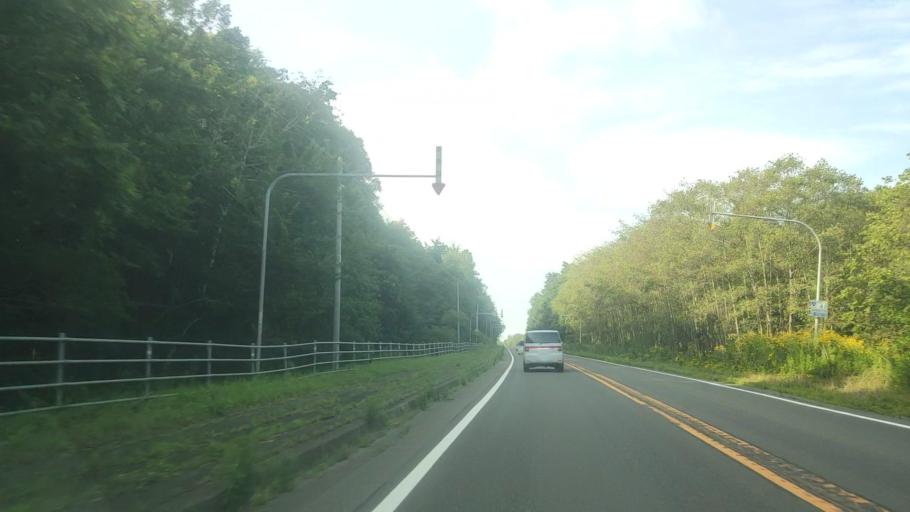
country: JP
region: Hokkaido
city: Chitose
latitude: 42.8629
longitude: 141.8225
